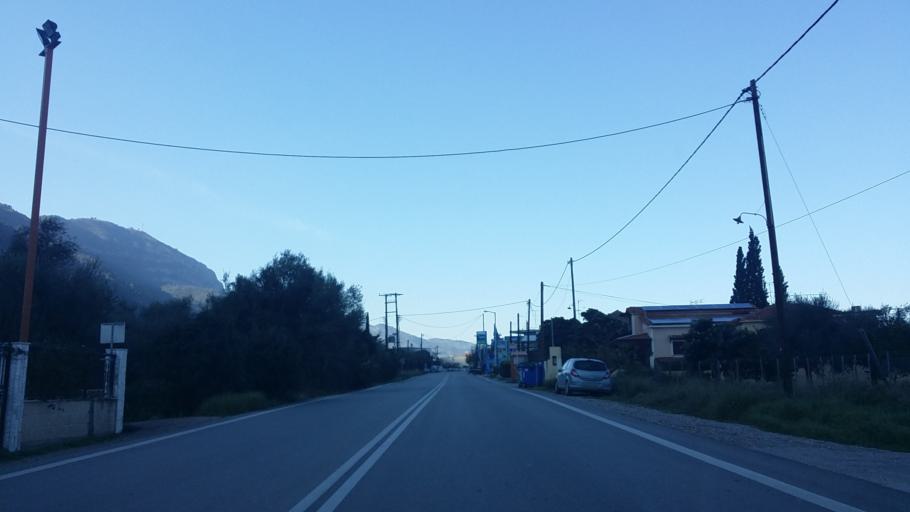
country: GR
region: West Greece
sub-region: Nomos Achaias
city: Temeni
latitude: 38.1834
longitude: 22.2038
